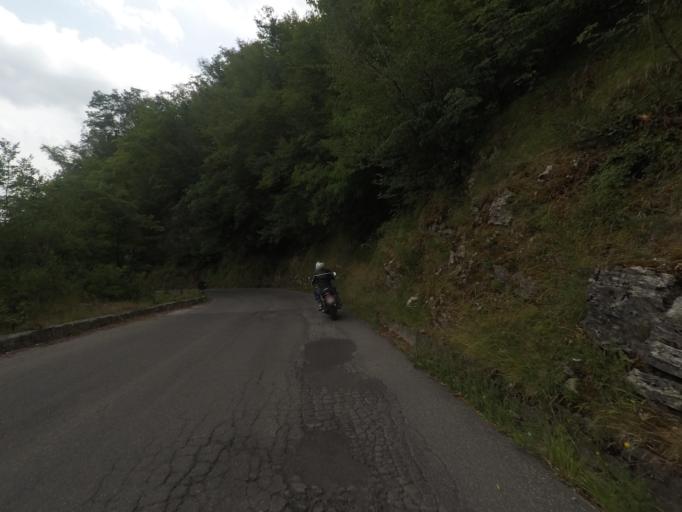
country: IT
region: Tuscany
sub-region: Provincia di Lucca
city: Castelnuovo di Garfagnana
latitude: 44.1109
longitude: 10.3682
